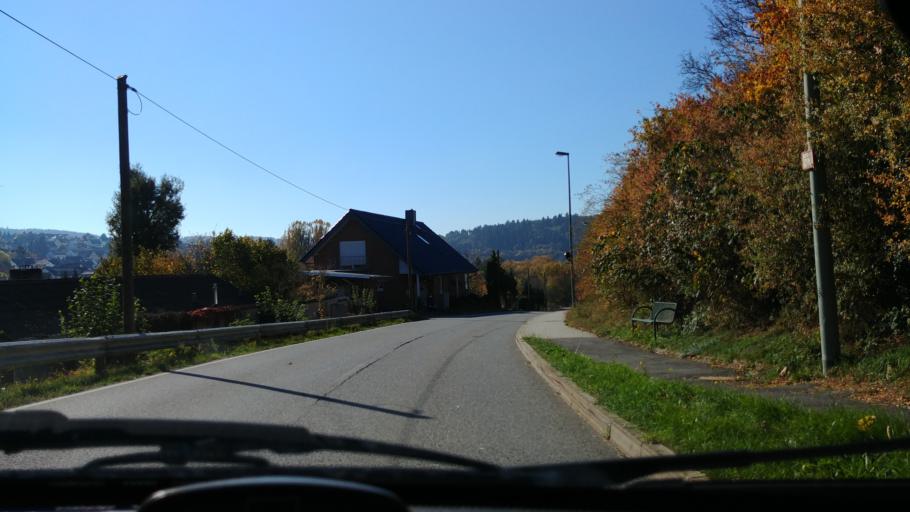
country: DE
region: Hesse
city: Taunusstein
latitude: 50.1423
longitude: 8.1429
